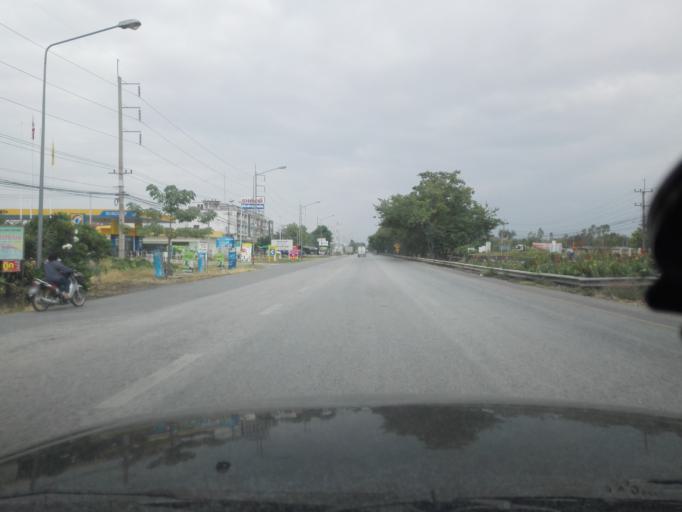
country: TH
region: Nakhon Sawan
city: Nakhon Sawan
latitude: 15.7260
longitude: 100.0427
